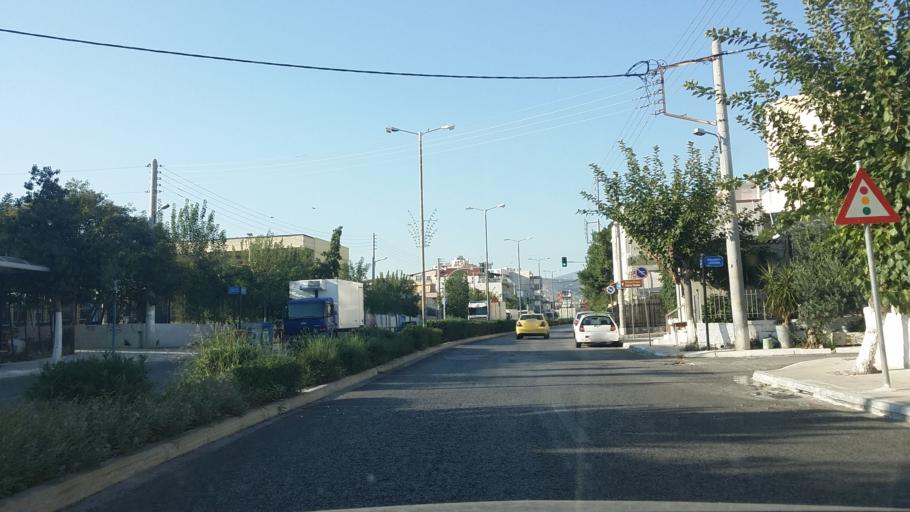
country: GR
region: Attica
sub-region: Nomarchia Athinas
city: Ilion
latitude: 38.0235
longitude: 23.7033
